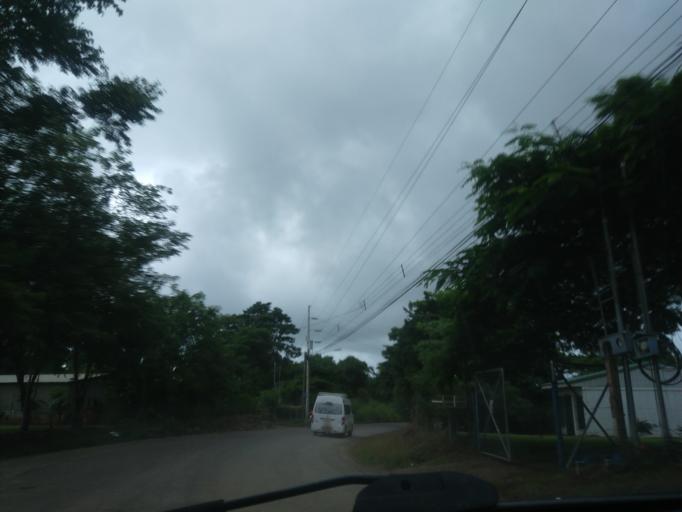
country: CR
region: Puntarenas
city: Paquera
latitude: 9.6539
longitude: -85.1256
